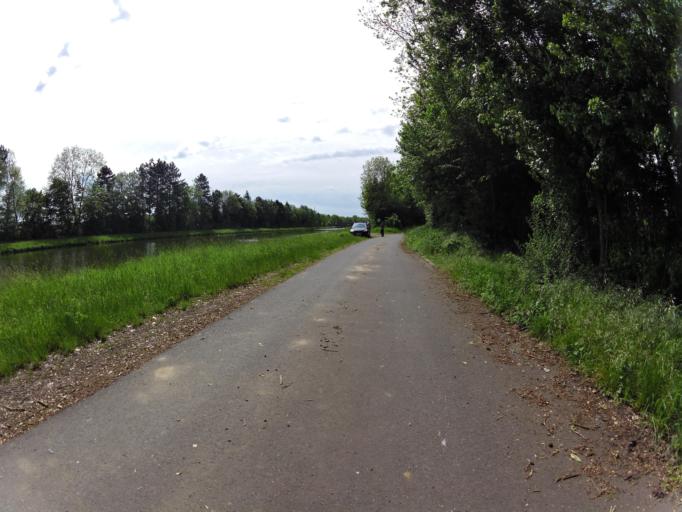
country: DE
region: Bavaria
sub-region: Regierungsbezirk Unterfranken
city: Volkach
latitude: 49.8573
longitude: 10.2233
